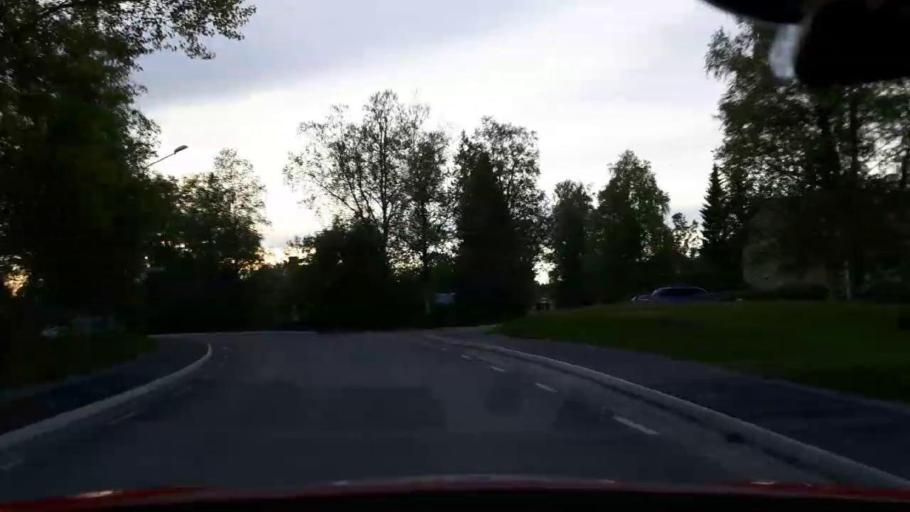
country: SE
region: Jaemtland
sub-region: OEstersunds Kommun
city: Ostersund
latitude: 62.9925
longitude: 14.5785
